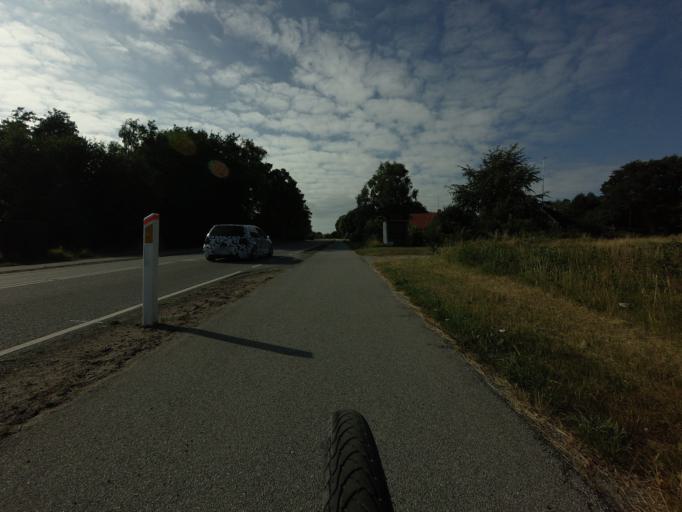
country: DK
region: North Denmark
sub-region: Laeso Kommune
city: Byrum
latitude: 57.2829
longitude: 10.9340
